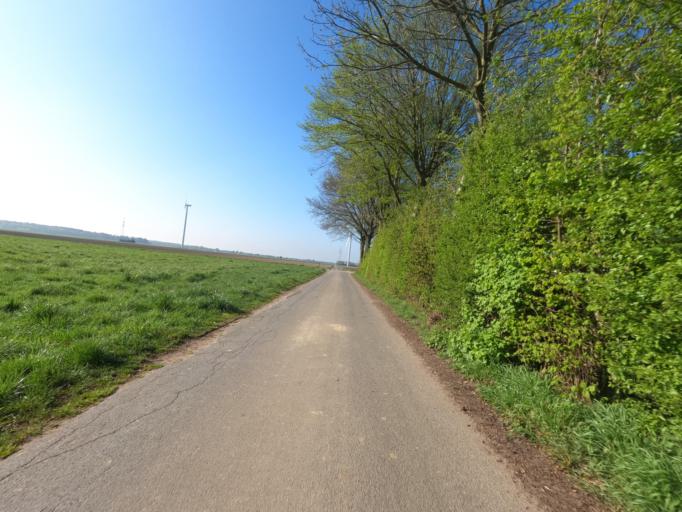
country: DE
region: North Rhine-Westphalia
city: Geilenkirchen
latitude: 51.0070
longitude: 6.0965
